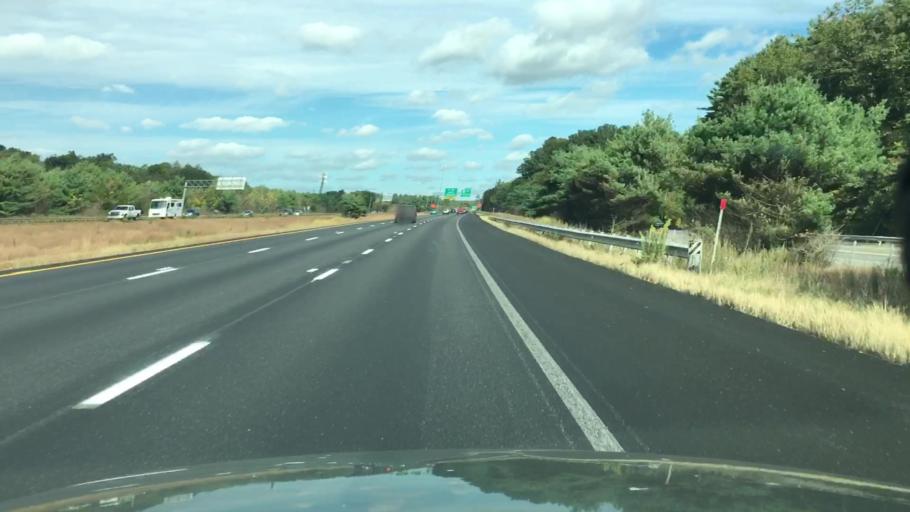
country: US
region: Massachusetts
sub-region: Worcester County
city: Sturbridge
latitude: 42.1049
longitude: -72.0839
